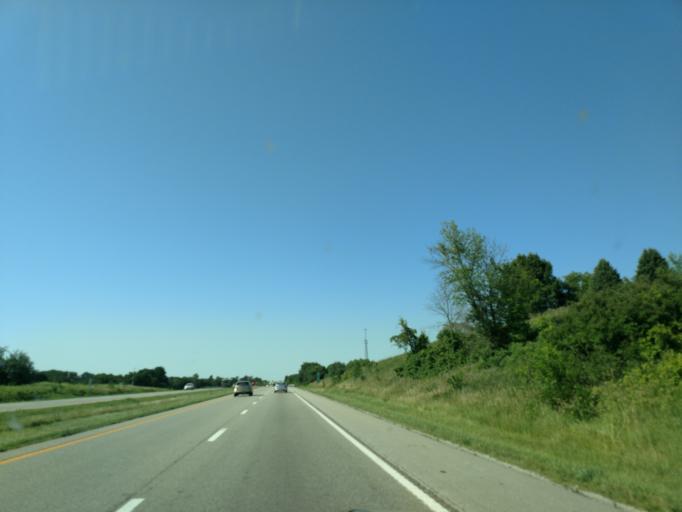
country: US
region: Missouri
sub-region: Buchanan County
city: Saint Joseph
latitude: 39.6231
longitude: -94.7882
